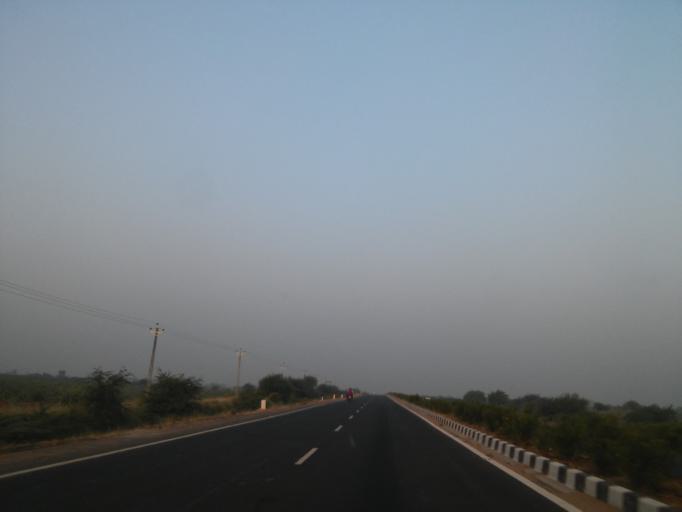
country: IN
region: Gujarat
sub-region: Surendranagar
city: Halvad
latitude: 23.0295
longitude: 70.9584
